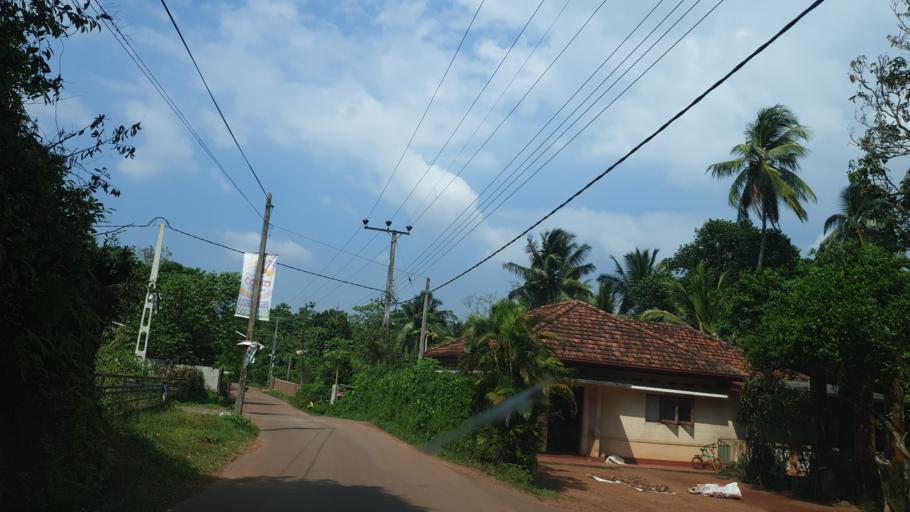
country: LK
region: Western
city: Panadura
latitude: 6.7319
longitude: 79.9530
